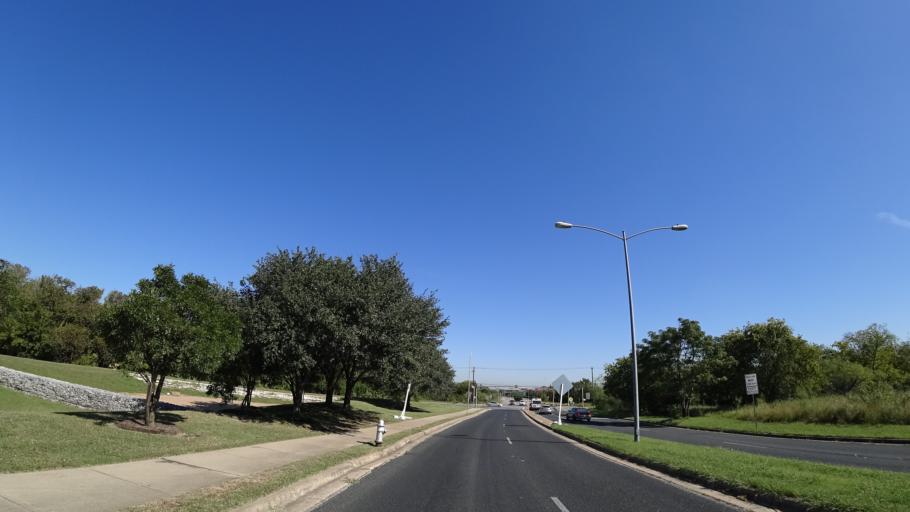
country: US
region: Texas
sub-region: Travis County
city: Austin
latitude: 30.2261
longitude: -97.7086
